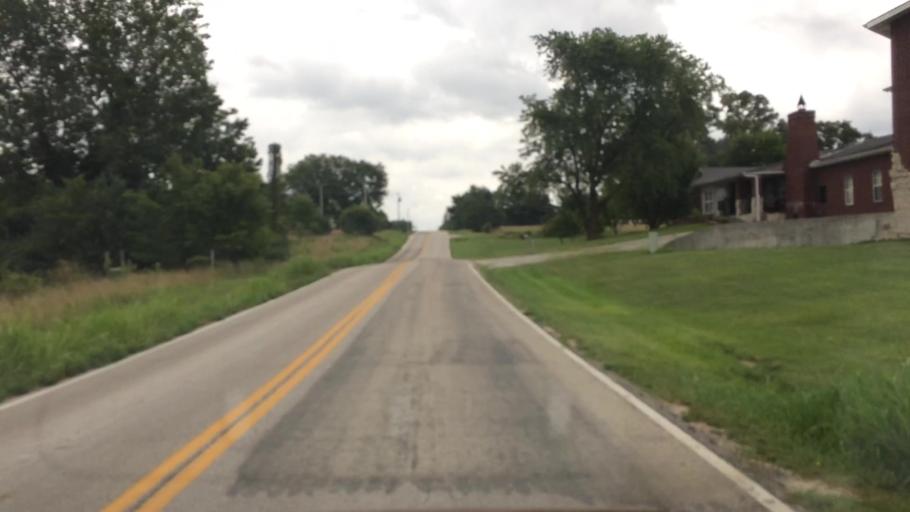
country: US
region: Missouri
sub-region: Webster County
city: Marshfield
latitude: 37.3413
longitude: -93.0041
